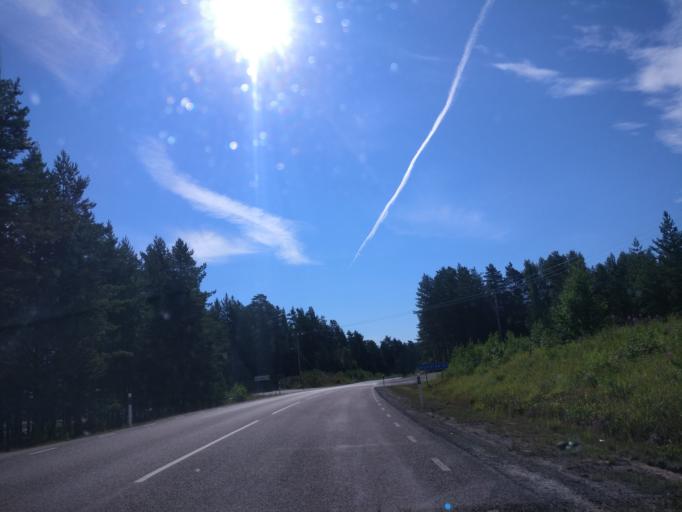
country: SE
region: Vaermland
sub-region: Hagfors Kommun
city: Hagfors
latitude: 60.0636
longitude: 13.7502
